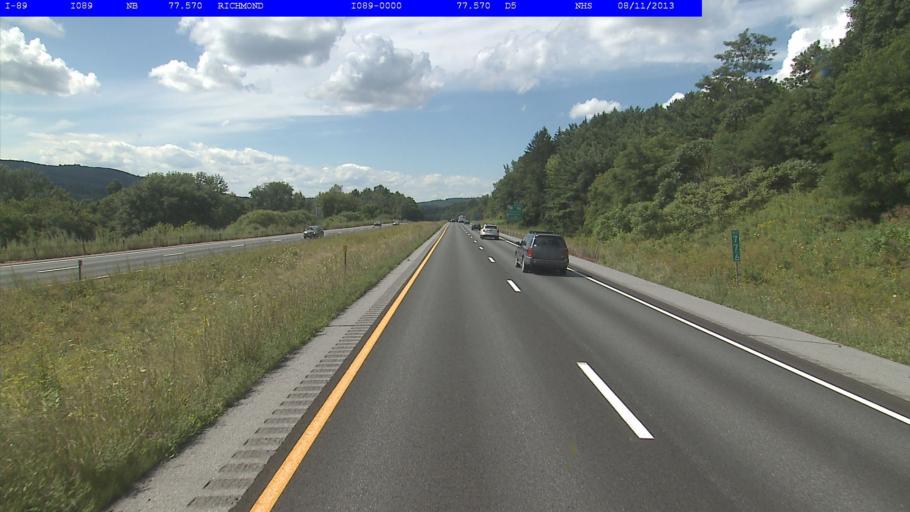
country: US
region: Vermont
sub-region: Chittenden County
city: Williston
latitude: 44.4175
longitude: -72.9972
